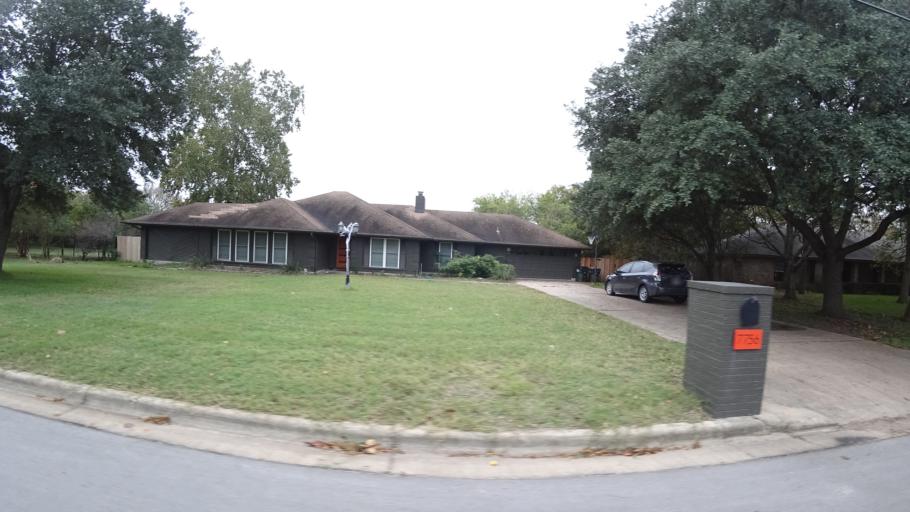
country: US
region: Texas
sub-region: Travis County
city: Shady Hollow
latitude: 30.2159
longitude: -97.9105
